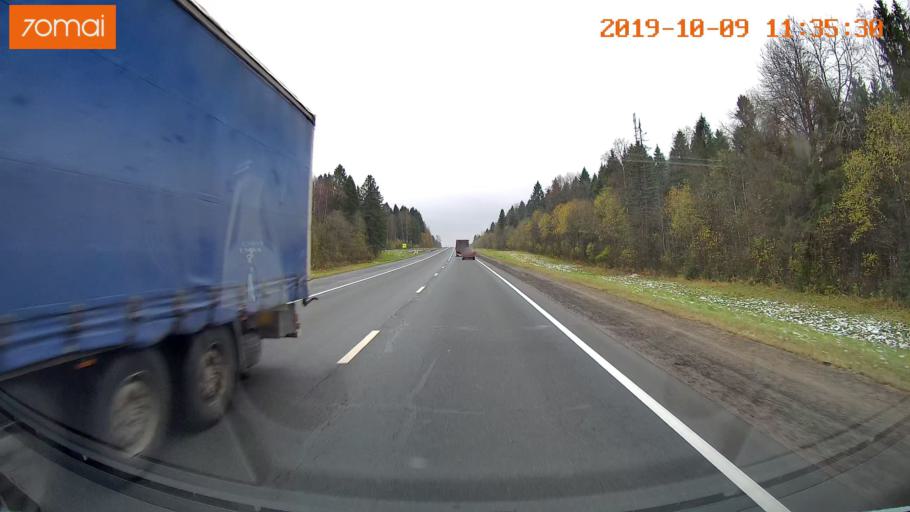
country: RU
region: Vologda
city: Gryazovets
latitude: 59.0025
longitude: 40.1267
